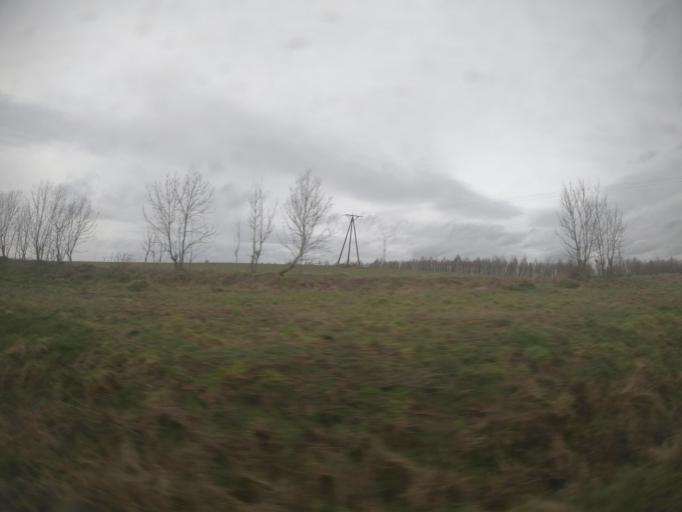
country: PL
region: West Pomeranian Voivodeship
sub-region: Powiat szczecinecki
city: Szczecinek
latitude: 53.7238
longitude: 16.8057
